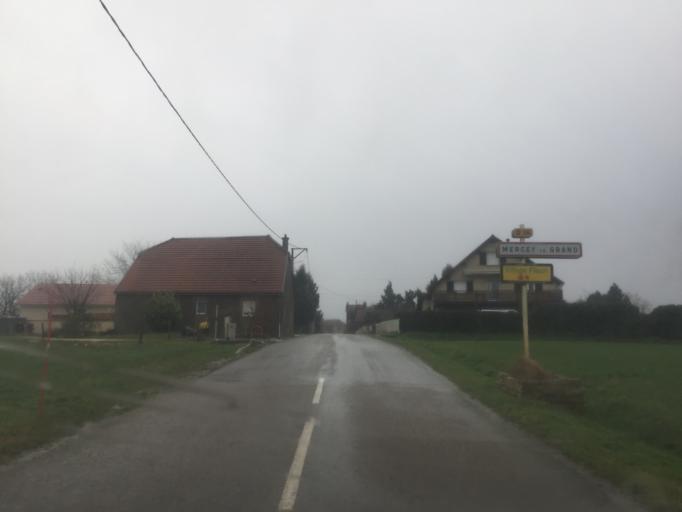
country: FR
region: Franche-Comte
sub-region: Departement du Jura
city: Dampierre
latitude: 47.2194
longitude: 5.7342
